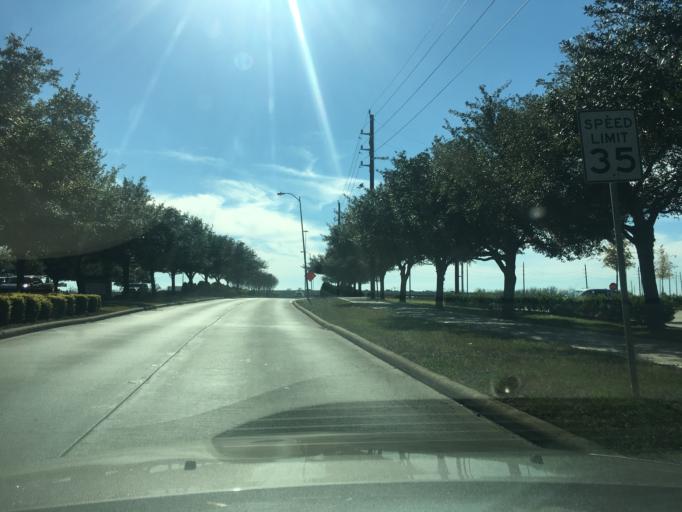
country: US
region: Texas
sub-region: Fort Bend County
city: Greatwood
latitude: 29.5597
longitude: -95.7156
